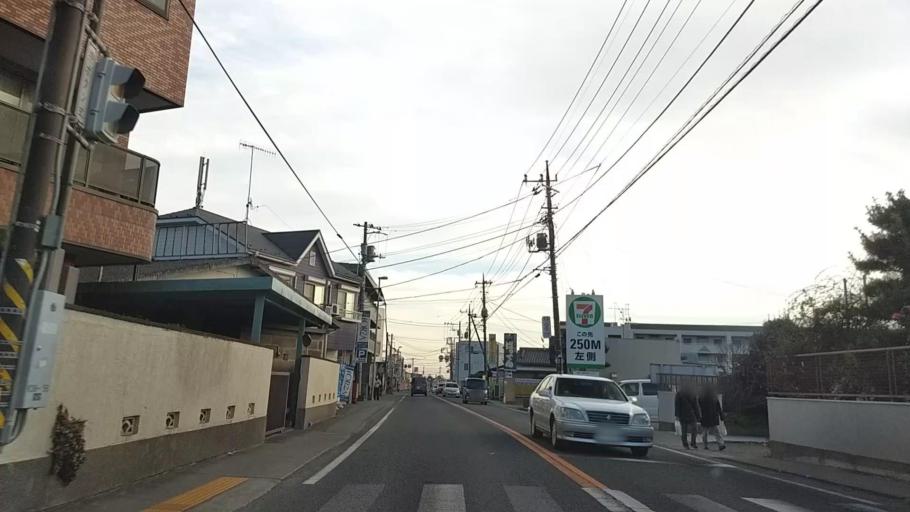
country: JP
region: Kanagawa
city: Atsugi
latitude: 35.4734
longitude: 139.3460
